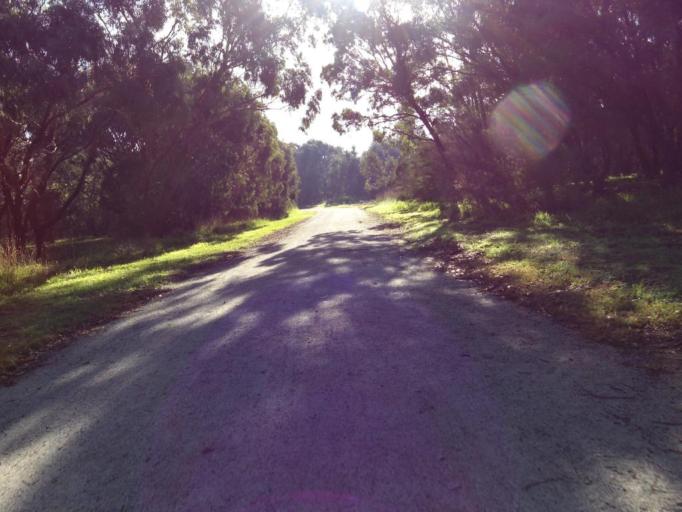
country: AU
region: Victoria
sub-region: Kingston
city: Dingley Village
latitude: -37.9908
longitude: 145.1208
